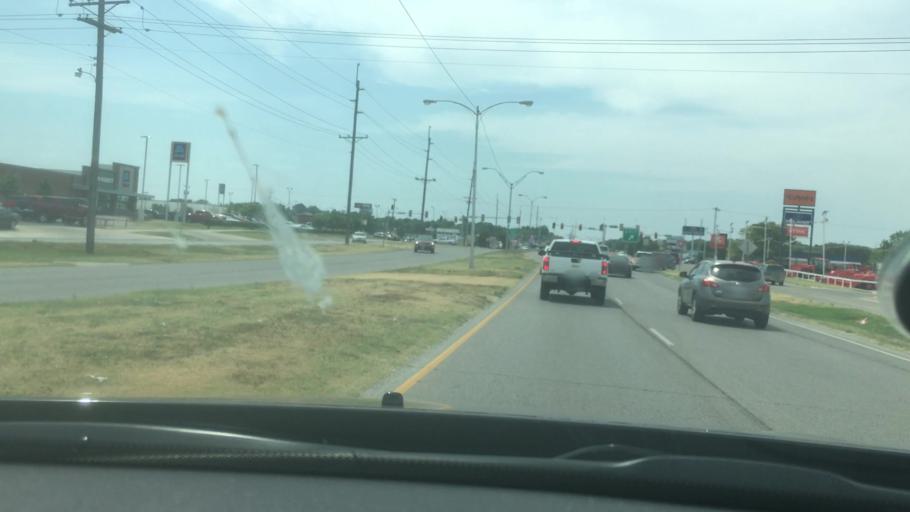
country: US
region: Oklahoma
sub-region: Carter County
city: Ardmore
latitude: 34.1820
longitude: -97.1431
